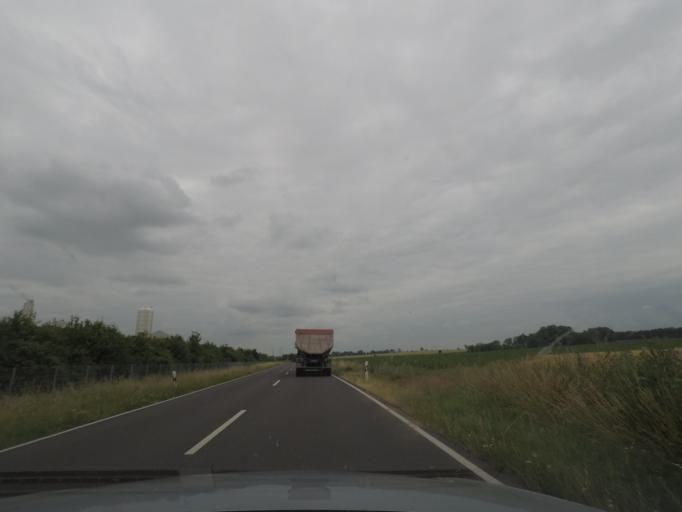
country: DE
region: Saxony-Anhalt
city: Erxleben
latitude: 52.2196
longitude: 11.3028
